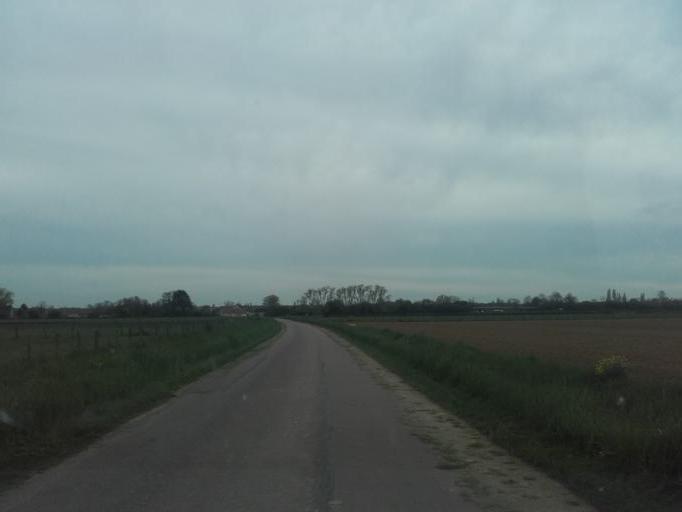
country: FR
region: Bourgogne
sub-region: Departement de la Cote-d'Or
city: Bligny-les-Beaune
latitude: 46.9844
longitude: 4.8516
